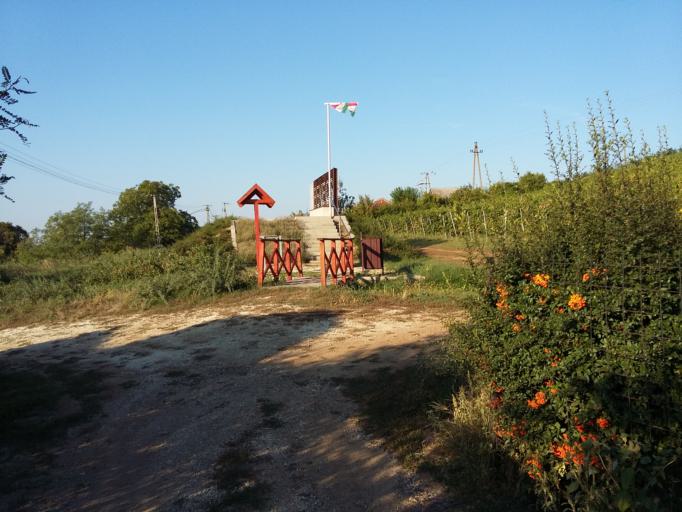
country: HU
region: Borsod-Abauj-Zemplen
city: Bekecs
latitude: 48.1541
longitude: 21.1737
